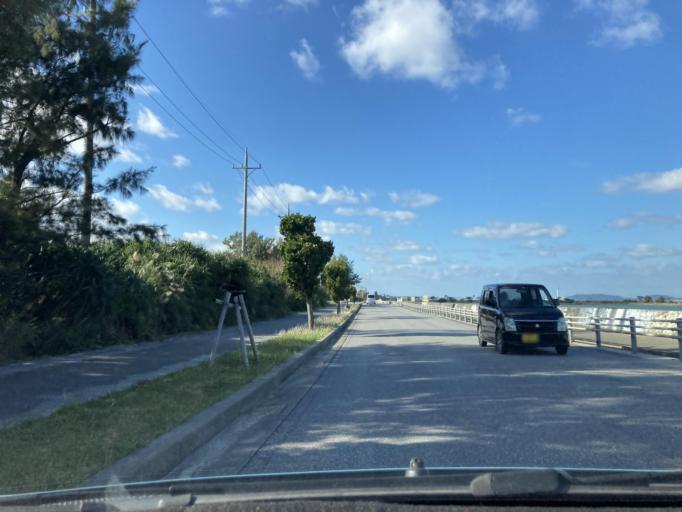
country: JP
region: Okinawa
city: Katsuren-haebaru
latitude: 26.3258
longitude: 127.9121
